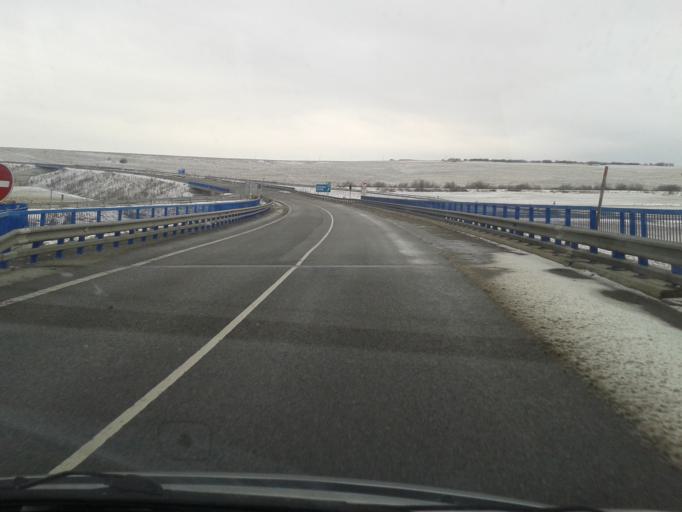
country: SK
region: Zilinsky
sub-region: Okres Zilina
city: Trstena
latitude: 49.3607
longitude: 19.6331
